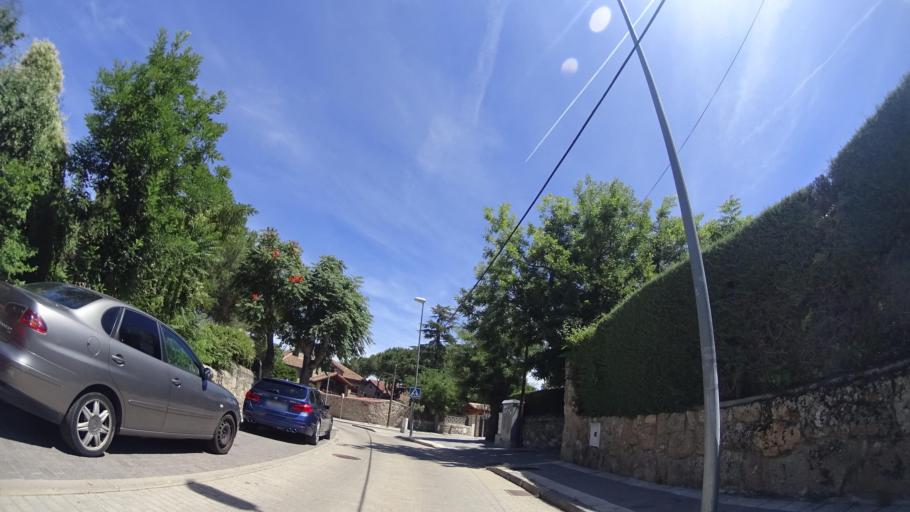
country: ES
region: Madrid
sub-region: Provincia de Madrid
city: Collado-Villalba
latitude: 40.6403
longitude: -3.9929
